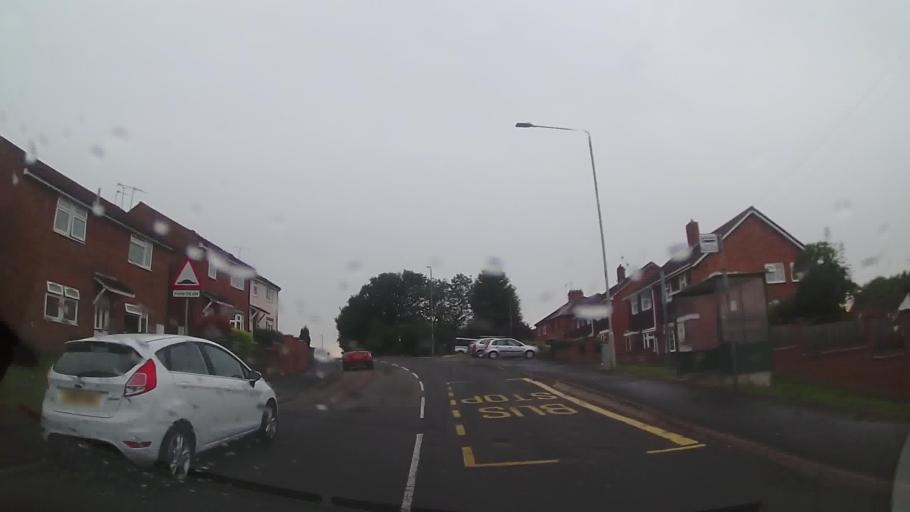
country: GB
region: England
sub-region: Leicestershire
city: Glenfield
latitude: 52.6450
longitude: -1.2031
